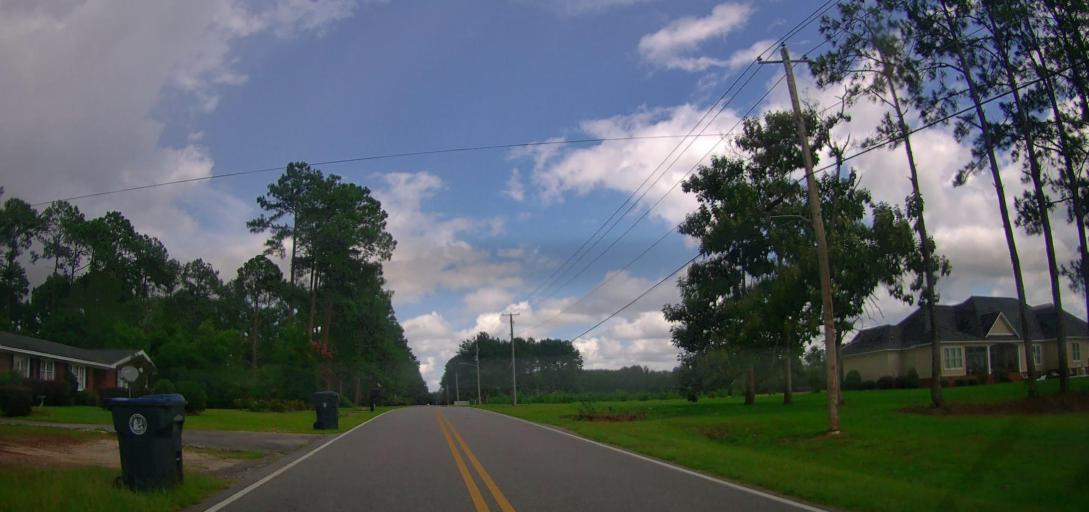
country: US
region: Georgia
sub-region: Ben Hill County
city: Fitzgerald
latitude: 31.7057
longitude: -83.2905
